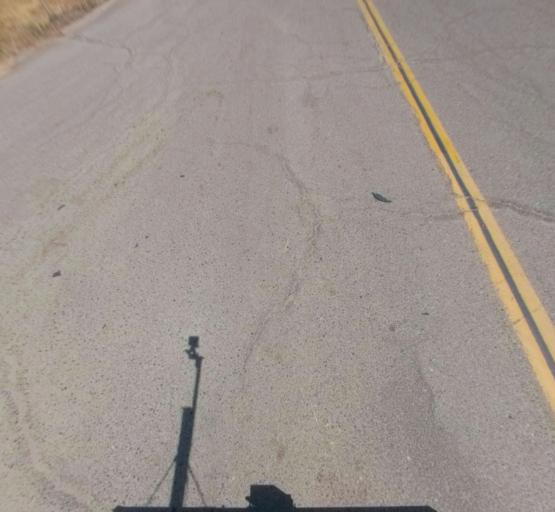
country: US
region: California
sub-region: Madera County
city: Chowchilla
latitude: 37.0837
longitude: -120.4371
